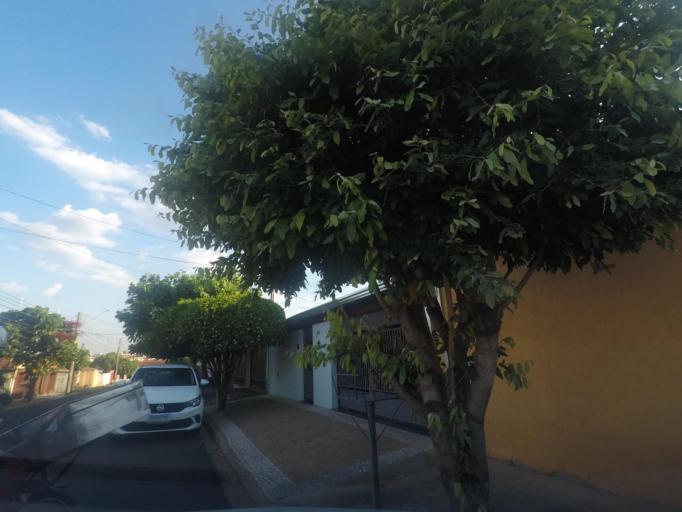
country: BR
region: Sao Paulo
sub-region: Sumare
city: Sumare
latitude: -22.8132
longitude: -47.2826
